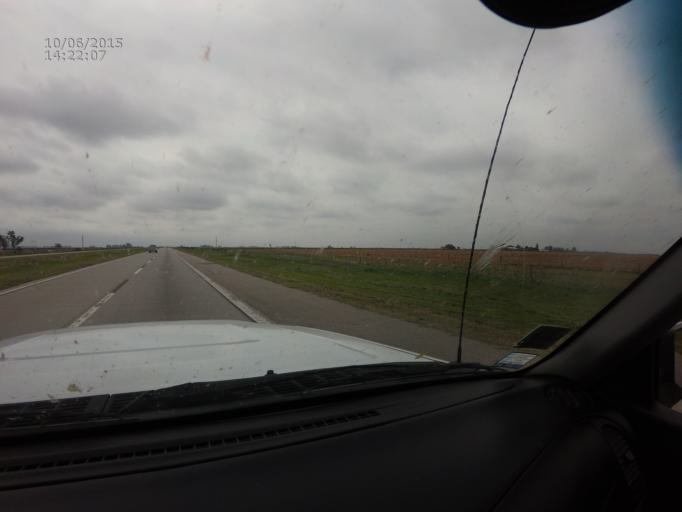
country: AR
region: Cordoba
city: Tio Pujio
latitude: -32.3179
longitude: -63.2746
